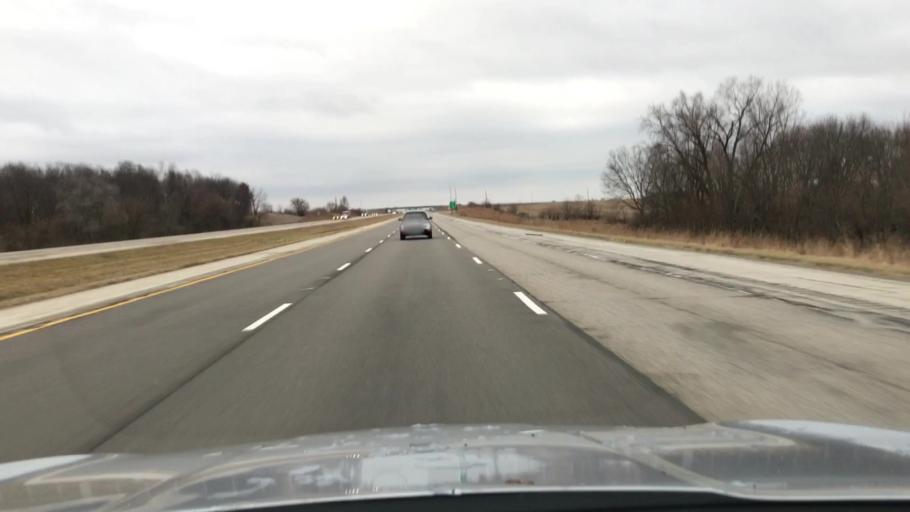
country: US
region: Illinois
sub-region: Logan County
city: Lincoln
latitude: 40.1228
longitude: -89.4169
